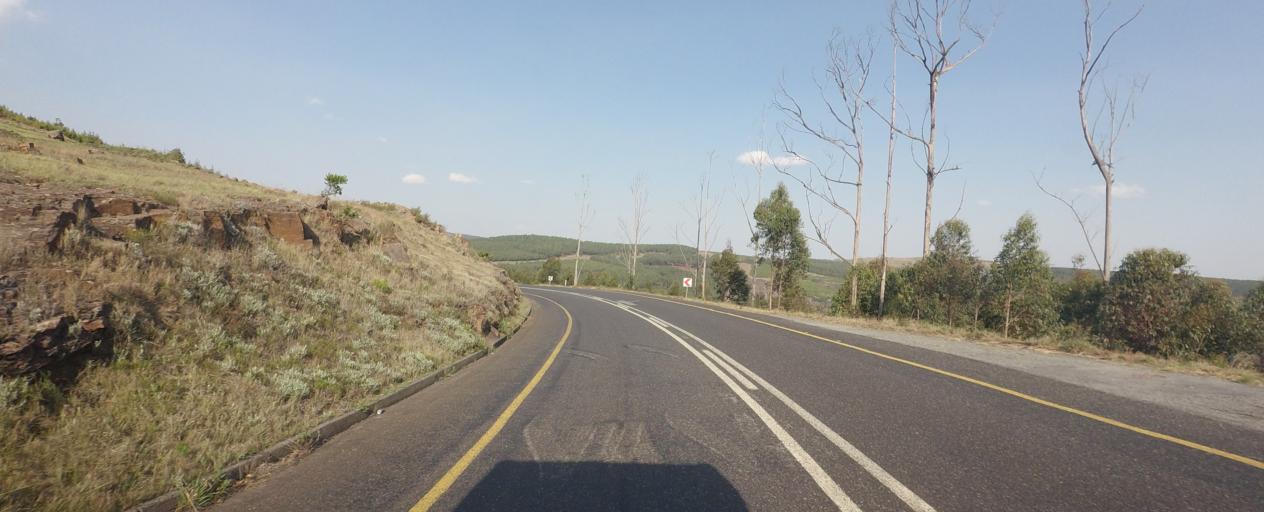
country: ZA
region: Mpumalanga
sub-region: Ehlanzeni District
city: Lydenburg
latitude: -25.1696
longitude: 30.6381
